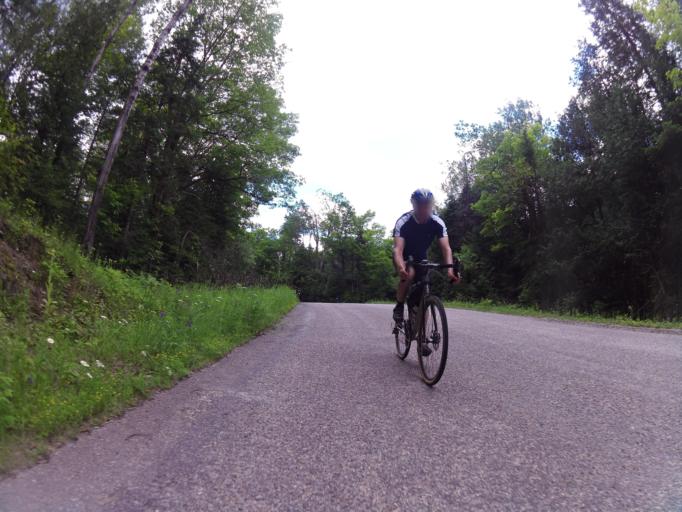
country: CA
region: Ontario
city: Renfrew
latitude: 45.0329
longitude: -76.7329
